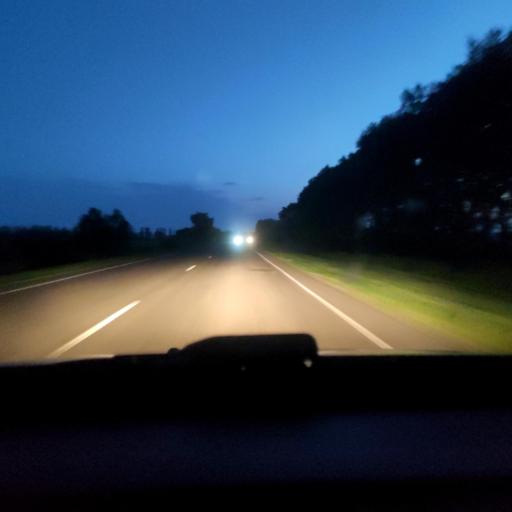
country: RU
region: Voronezj
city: Panino
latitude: 51.6296
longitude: 40.0549
